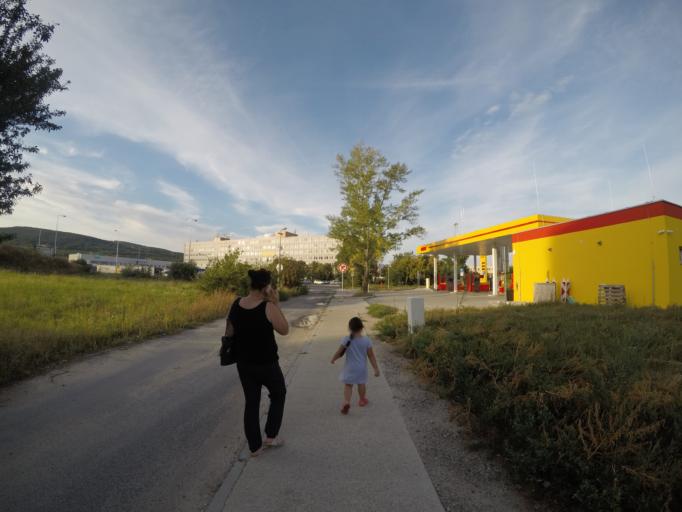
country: SK
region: Bratislavsky
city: Svaty Jur
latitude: 48.2184
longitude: 17.1825
